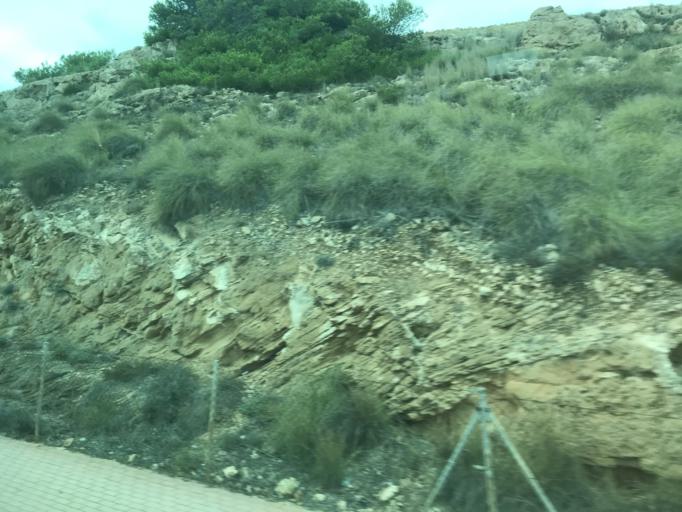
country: ES
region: Valencia
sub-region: Provincia de Alicante
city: Torrevieja
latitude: 38.0007
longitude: -0.6506
